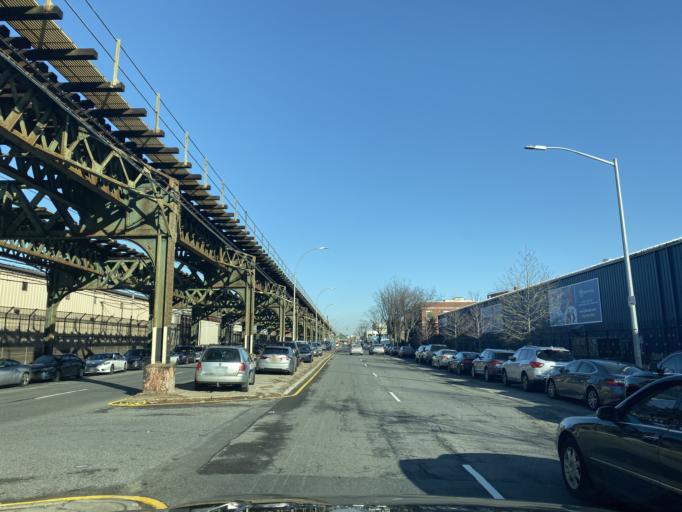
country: US
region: New York
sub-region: Kings County
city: Coney Island
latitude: 40.5841
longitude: -73.9744
